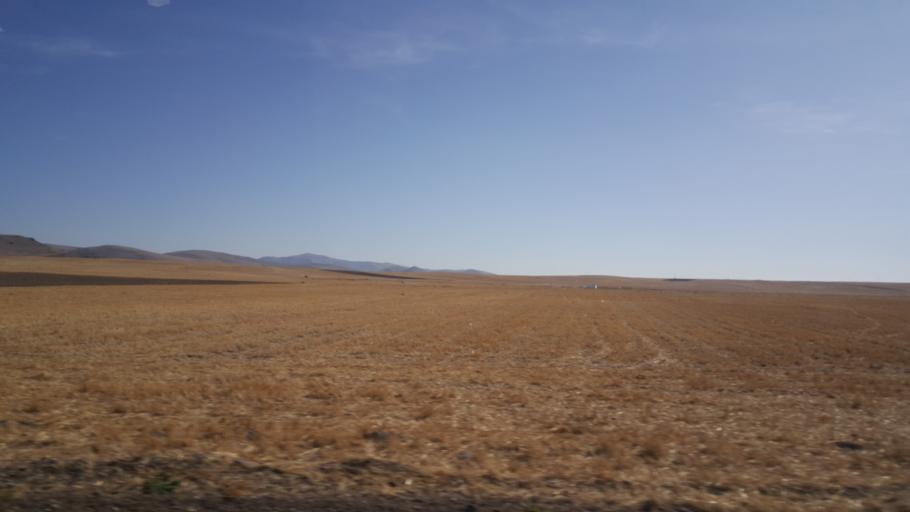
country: TR
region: Ankara
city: Yenice
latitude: 39.3456
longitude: 32.7582
